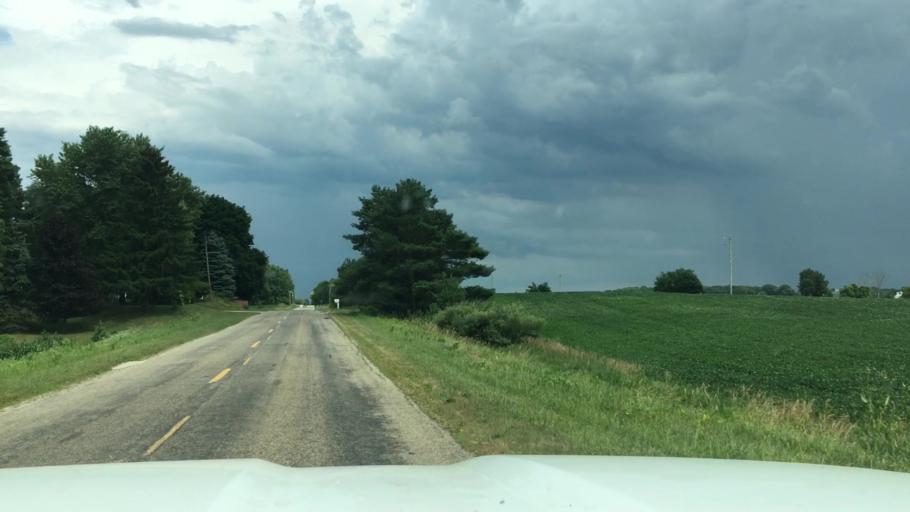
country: US
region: Michigan
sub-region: Montcalm County
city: Carson City
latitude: 43.2486
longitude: -84.7717
